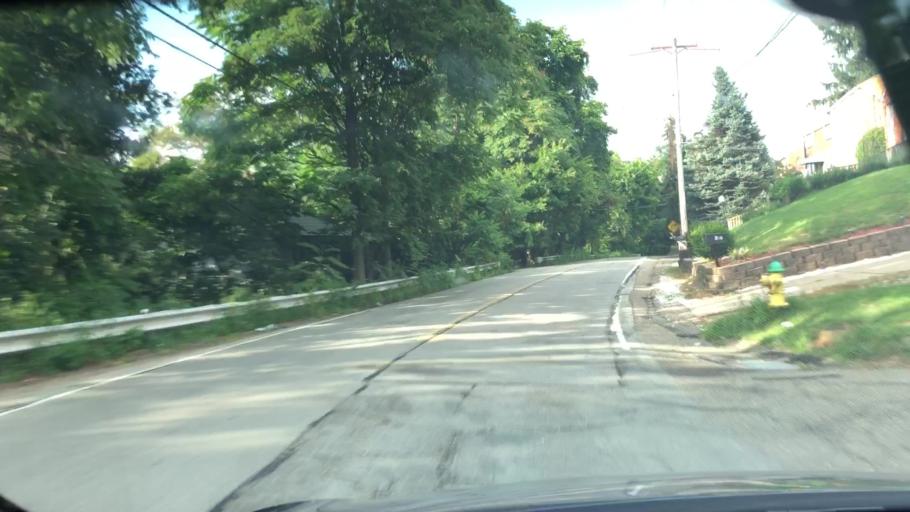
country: US
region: Pennsylvania
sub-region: Allegheny County
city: Blawnox
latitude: 40.4760
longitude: -79.8724
